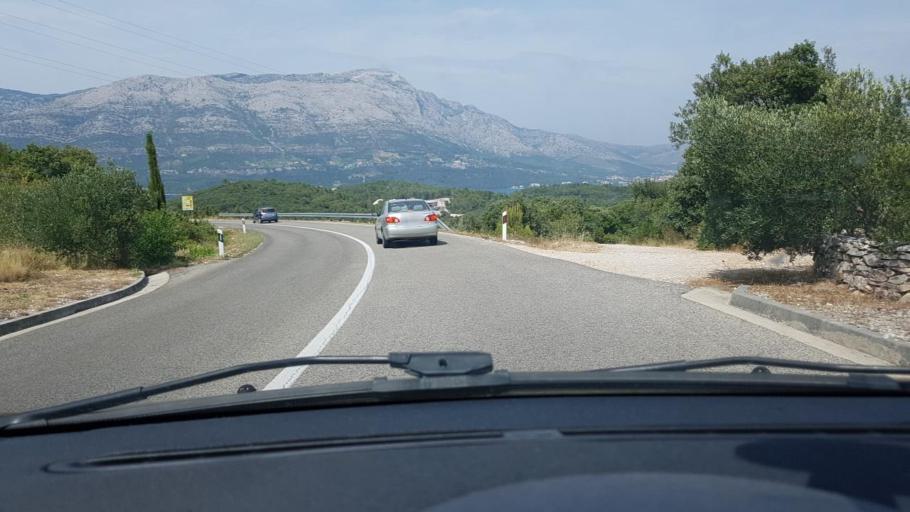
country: HR
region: Dubrovacko-Neretvanska
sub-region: Grad Korcula
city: Zrnovo
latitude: 42.9454
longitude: 17.1194
